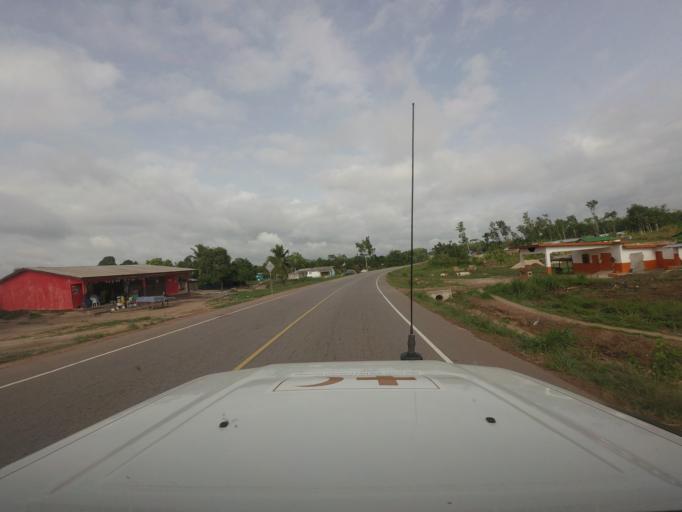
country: LR
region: Bong
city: Gbarnga
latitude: 7.0017
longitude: -9.2904
